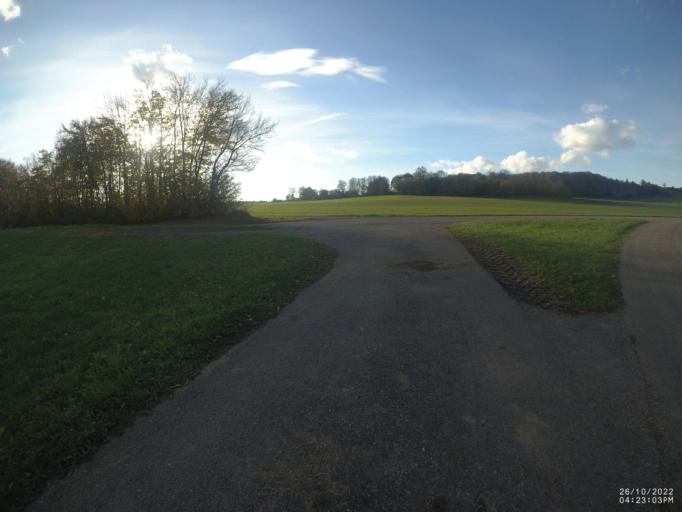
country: DE
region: Baden-Wuerttemberg
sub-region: Regierungsbezirk Stuttgart
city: Hohenstadt
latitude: 48.5339
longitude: 9.6696
